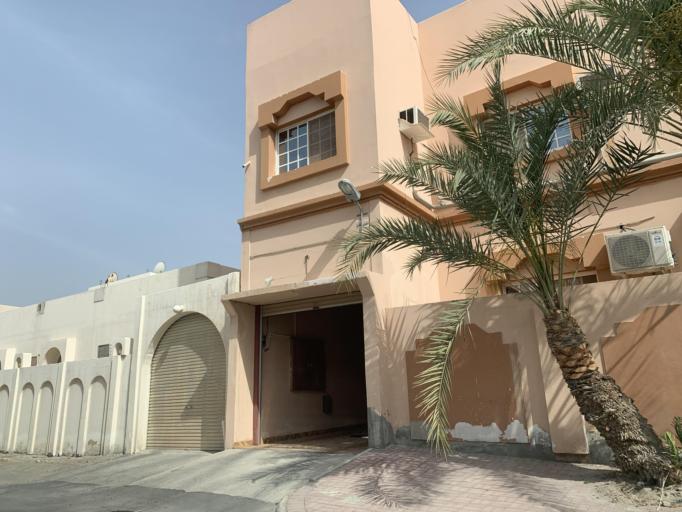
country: BH
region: Northern
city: Madinat `Isa
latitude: 26.1714
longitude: 50.5651
